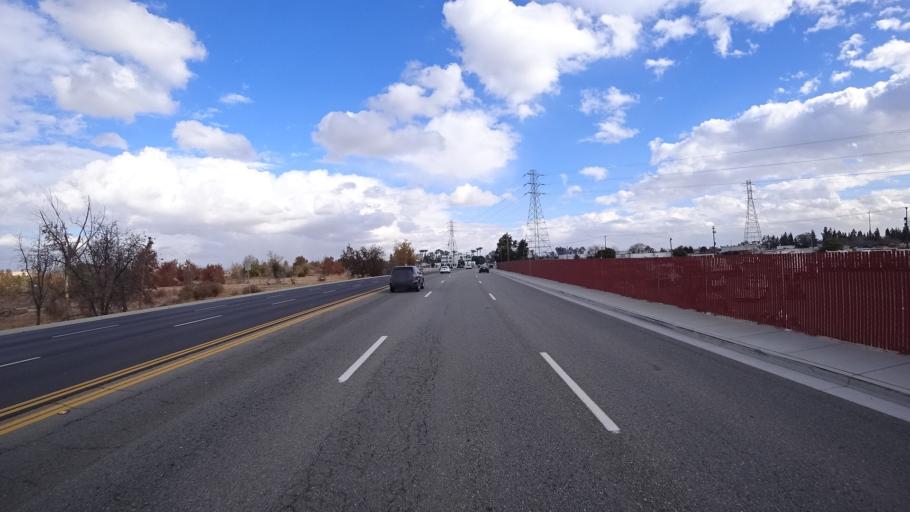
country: US
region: California
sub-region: Kern County
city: Bakersfield
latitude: 35.3727
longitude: -119.0521
